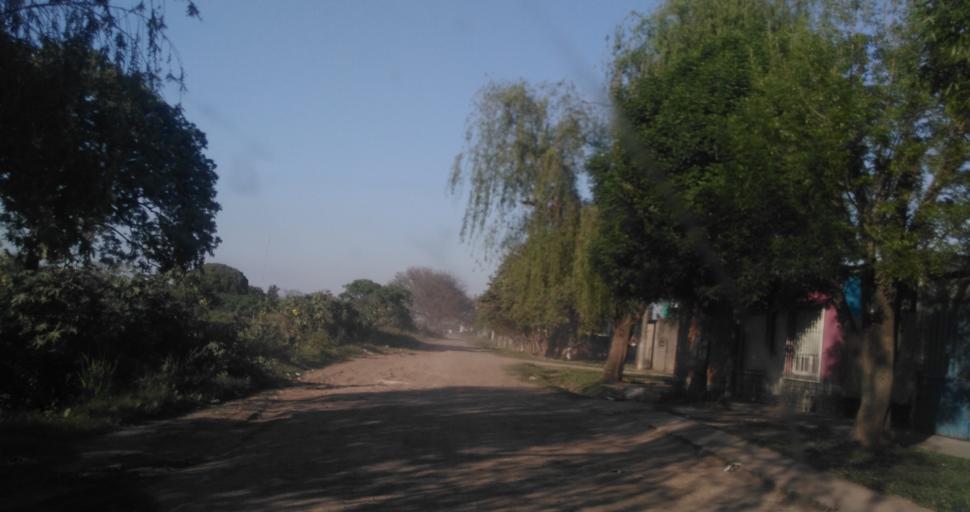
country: AR
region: Chaco
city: Fontana
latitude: -27.4121
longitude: -59.0322
